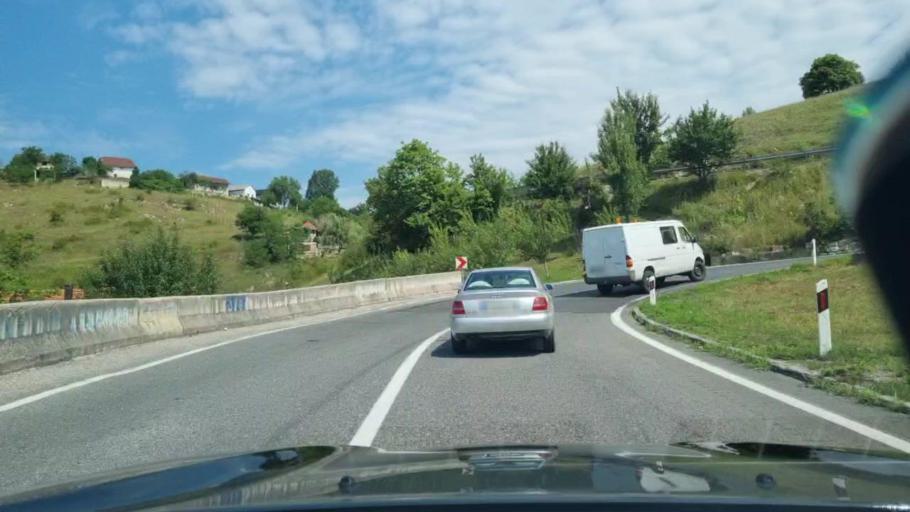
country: BA
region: Federation of Bosnia and Herzegovina
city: Izacic
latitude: 44.8694
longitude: 15.7847
